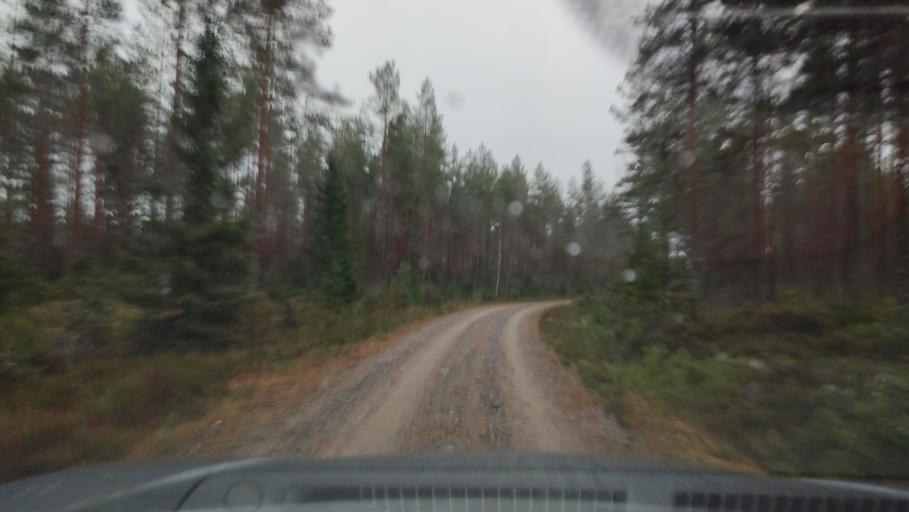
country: FI
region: Southern Ostrobothnia
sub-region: Suupohja
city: Karijoki
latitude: 62.1852
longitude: 21.7363
